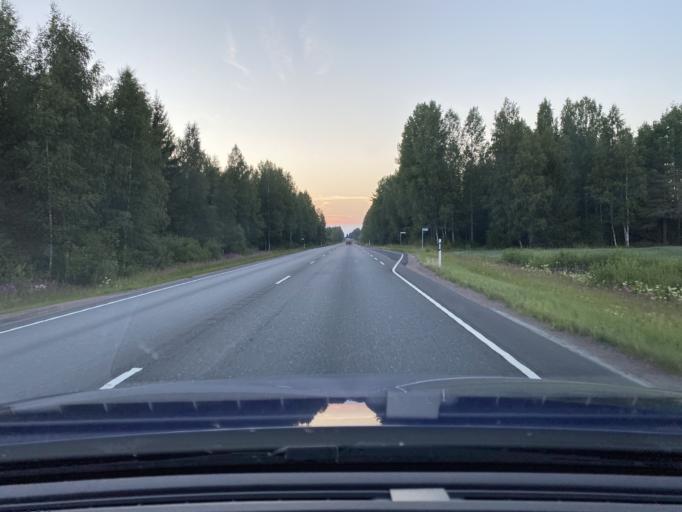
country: FI
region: Pirkanmaa
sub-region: Luoteis-Pirkanmaa
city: Ikaalinen
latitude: 61.8247
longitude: 22.9468
